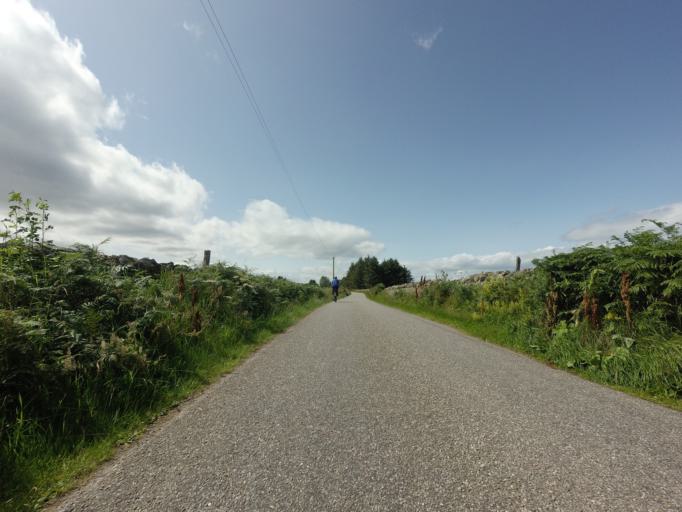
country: GB
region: Scotland
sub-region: Highland
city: Fortrose
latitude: 57.4910
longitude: -4.0150
